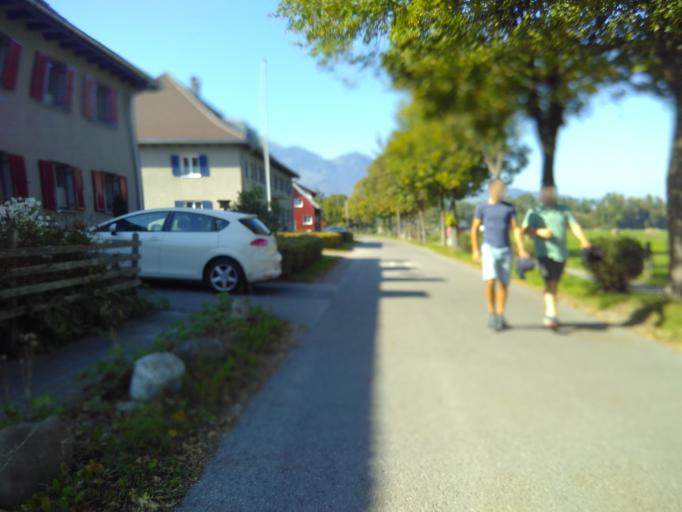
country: AT
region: Vorarlberg
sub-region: Politischer Bezirk Feldkirch
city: Nofels
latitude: 47.2566
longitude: 9.5759
